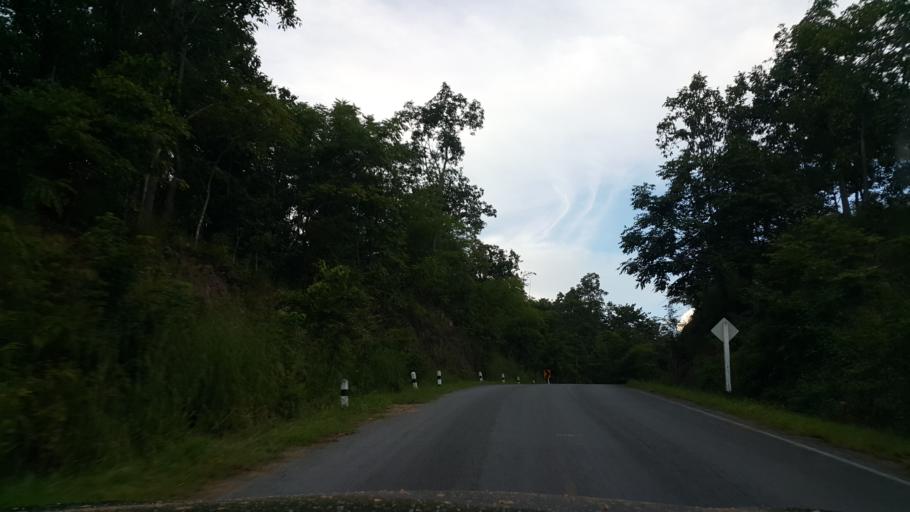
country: TH
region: Mae Hong Son
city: Mae Hi
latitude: 19.2146
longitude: 98.4314
